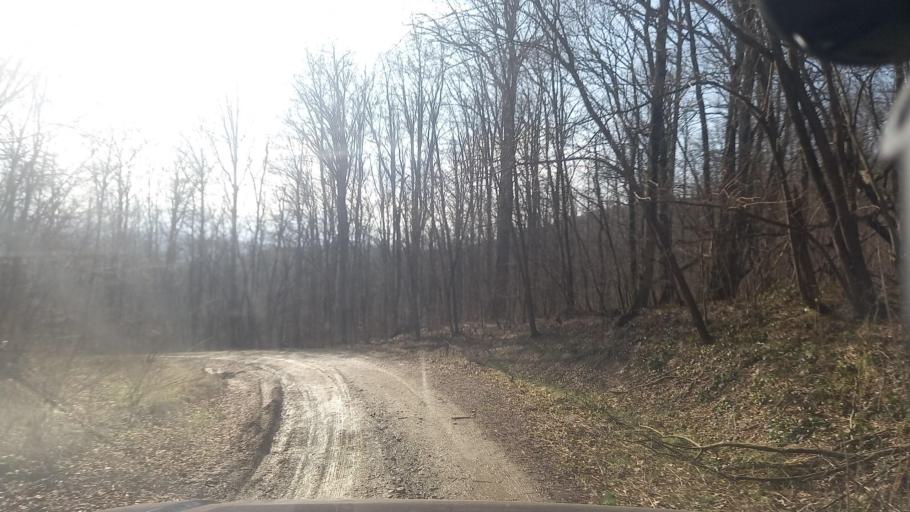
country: RU
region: Krasnodarskiy
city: Smolenskaya
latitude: 44.7127
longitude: 38.7796
